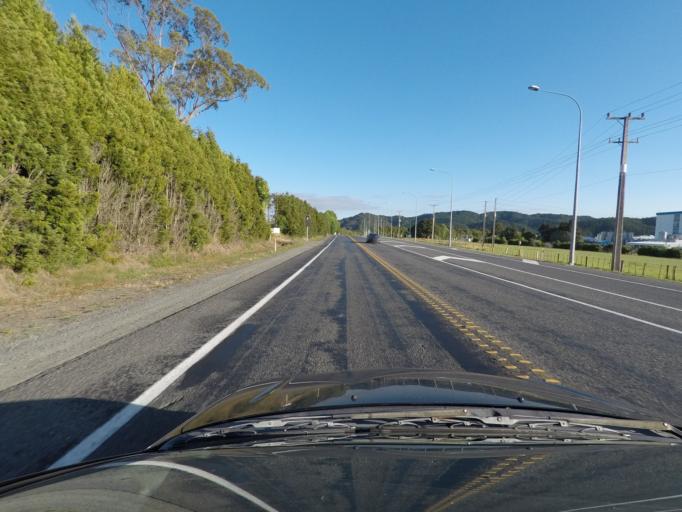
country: NZ
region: Northland
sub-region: Whangarei
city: Whangarei
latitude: -35.6371
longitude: 174.2965
